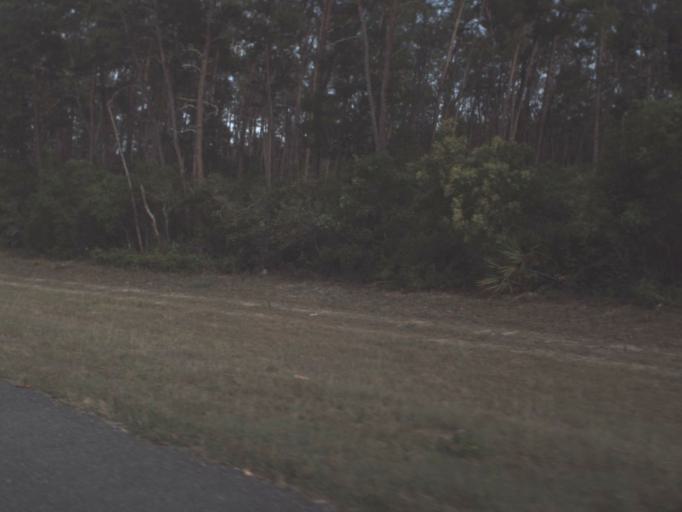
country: US
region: Florida
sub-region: Lake County
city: Astor
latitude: 29.1774
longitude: -81.7606
